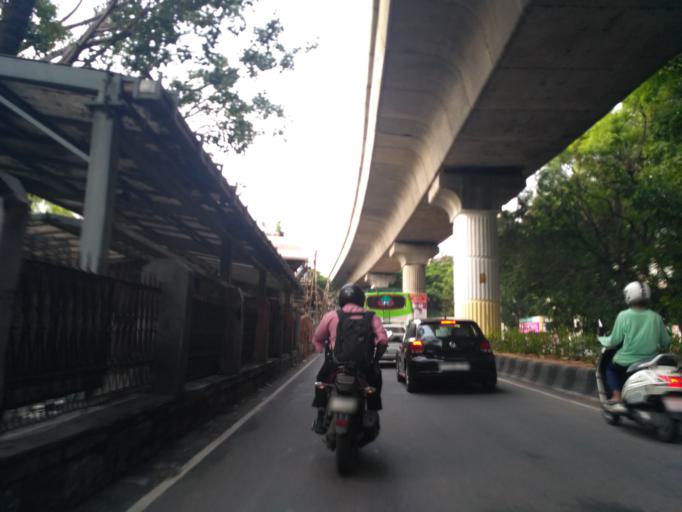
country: IN
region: Karnataka
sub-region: Bangalore Urban
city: Bangalore
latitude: 12.9670
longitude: 77.5359
